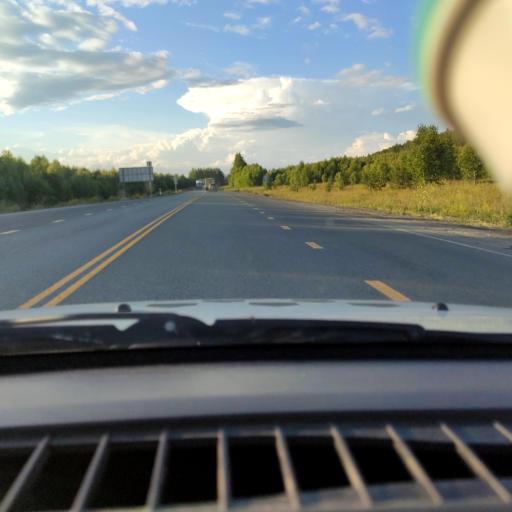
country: RU
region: Chelyabinsk
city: Karabash
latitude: 55.3620
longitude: 60.2444
